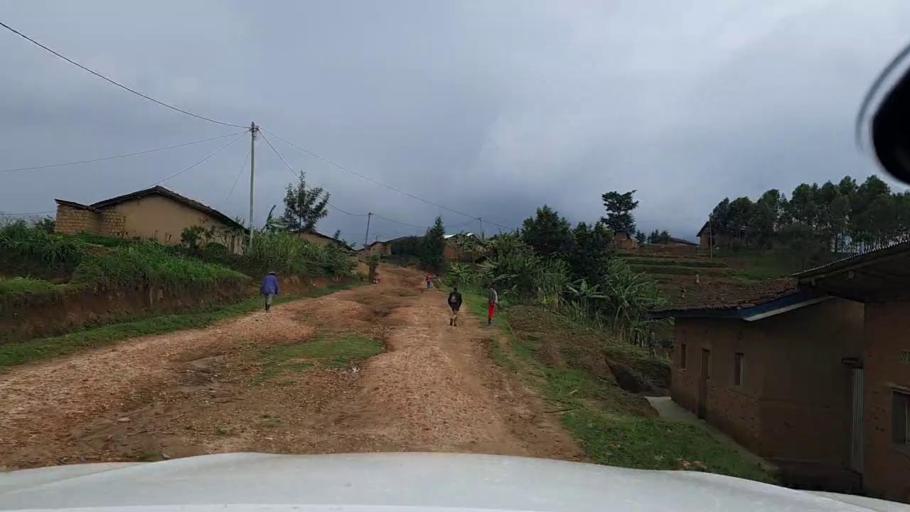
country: RW
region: Western Province
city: Kibuye
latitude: -2.1052
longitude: 29.4842
